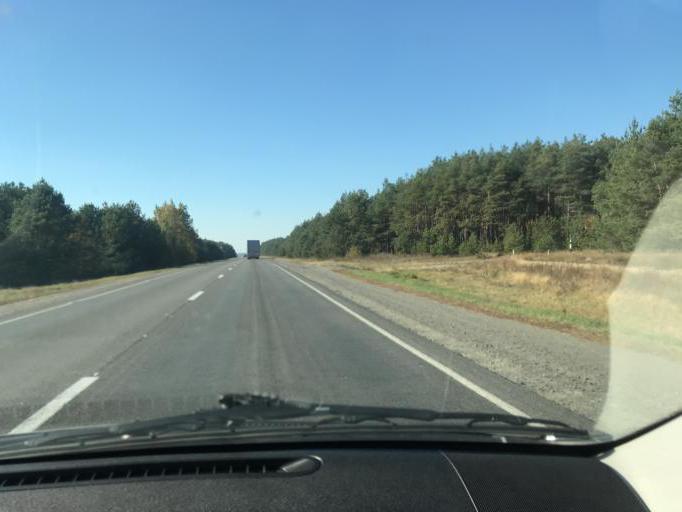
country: BY
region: Brest
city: Davyd-Haradok
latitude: 52.2380
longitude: 27.2213
